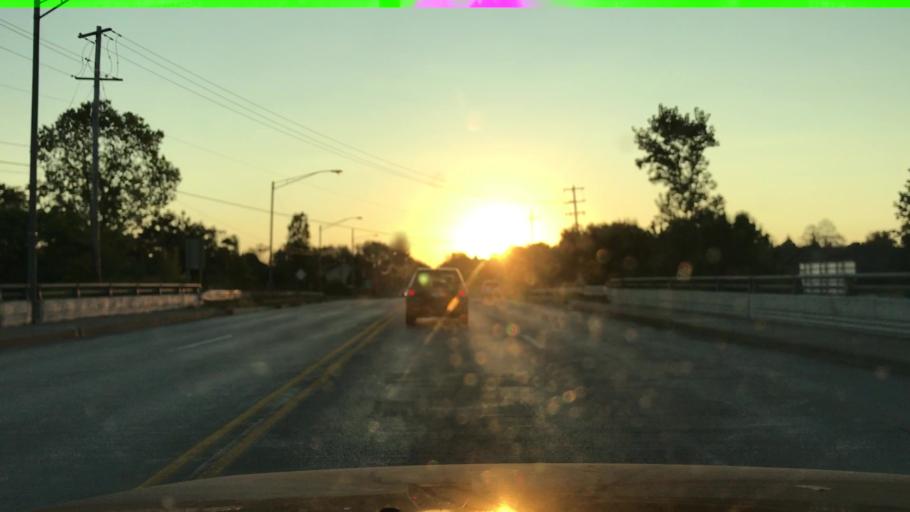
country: US
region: Michigan
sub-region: Kent County
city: East Grand Rapids
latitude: 42.9844
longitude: -85.6049
